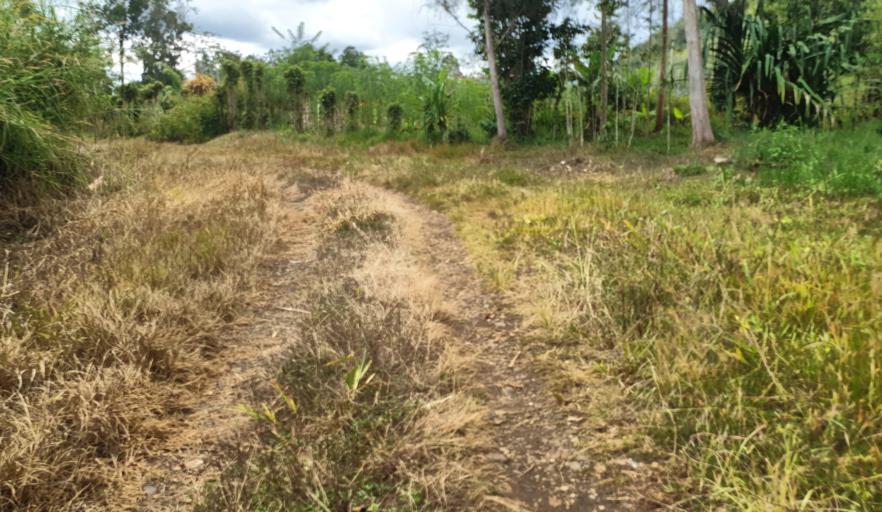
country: PG
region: Jiwaka
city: Minj
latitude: -5.9133
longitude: 144.8240
